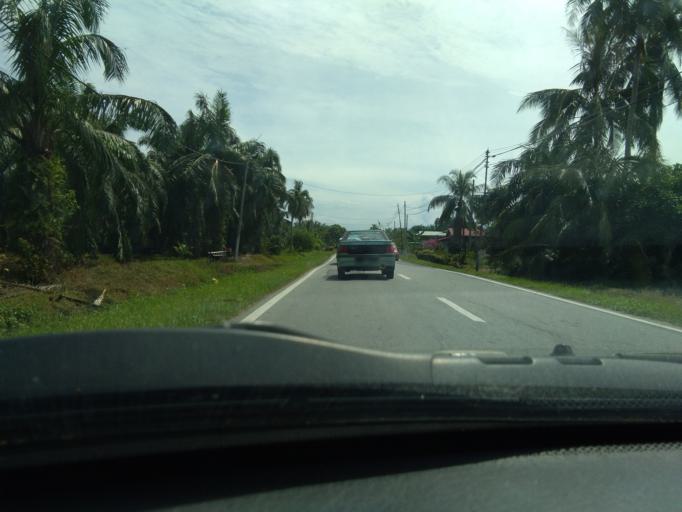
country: MY
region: Perak
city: Bagan Serai
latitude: 5.0285
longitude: 100.5577
